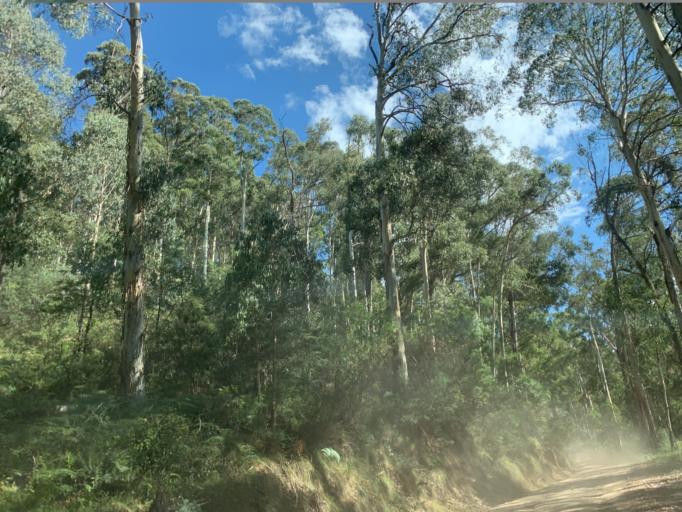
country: AU
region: Victoria
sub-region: Mansfield
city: Mansfield
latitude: -37.0955
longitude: 146.5158
